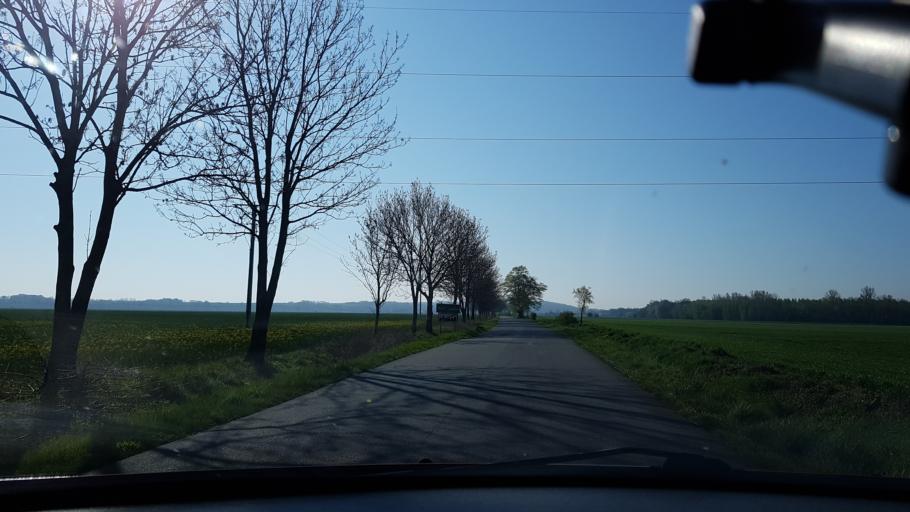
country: PL
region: Opole Voivodeship
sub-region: Powiat nyski
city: Nysa
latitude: 50.4277
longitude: 17.3078
